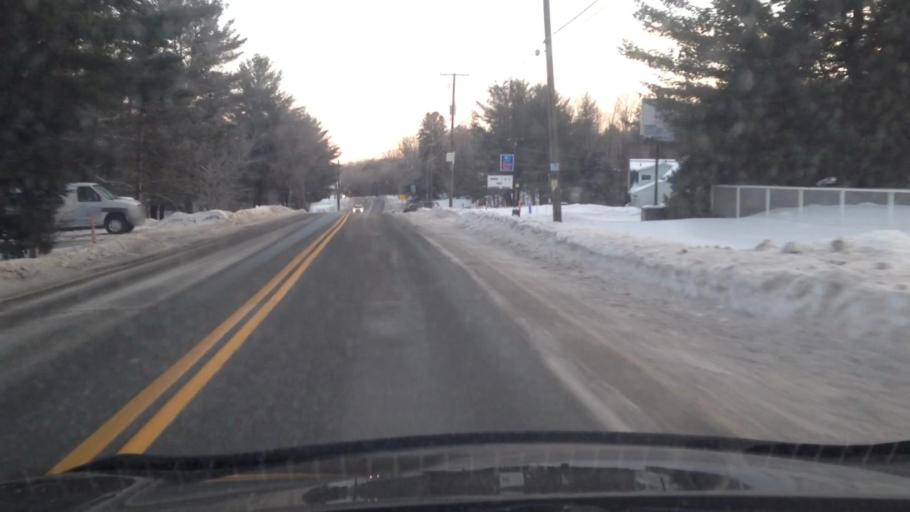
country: CA
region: Quebec
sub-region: Lanaudiere
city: Sainte-Julienne
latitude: 45.9491
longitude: -73.7342
